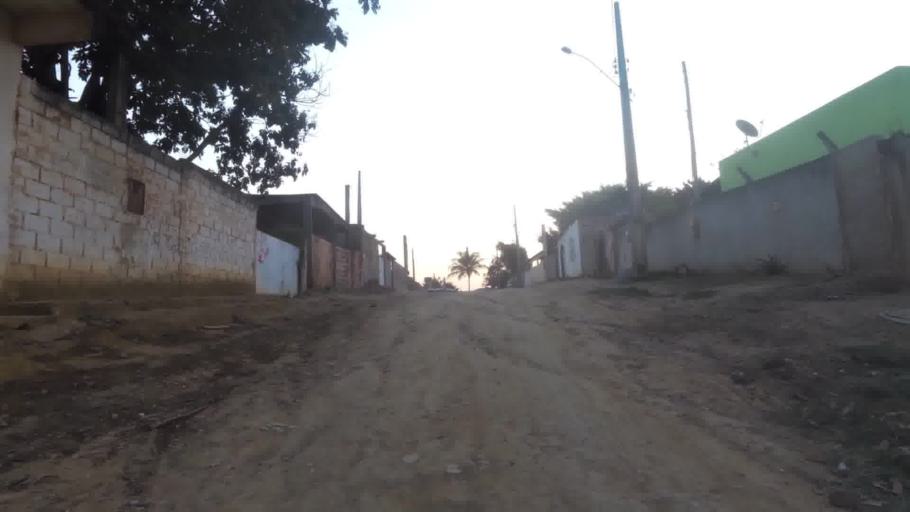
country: BR
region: Espirito Santo
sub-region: Piuma
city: Piuma
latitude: -20.8270
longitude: -40.7205
